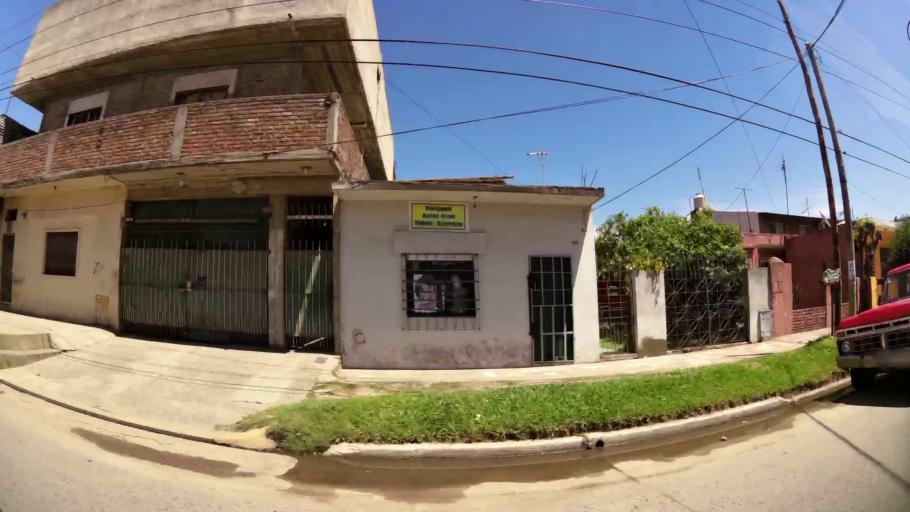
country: AR
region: Buenos Aires
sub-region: Partido de Quilmes
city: Quilmes
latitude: -34.7198
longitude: -58.3190
